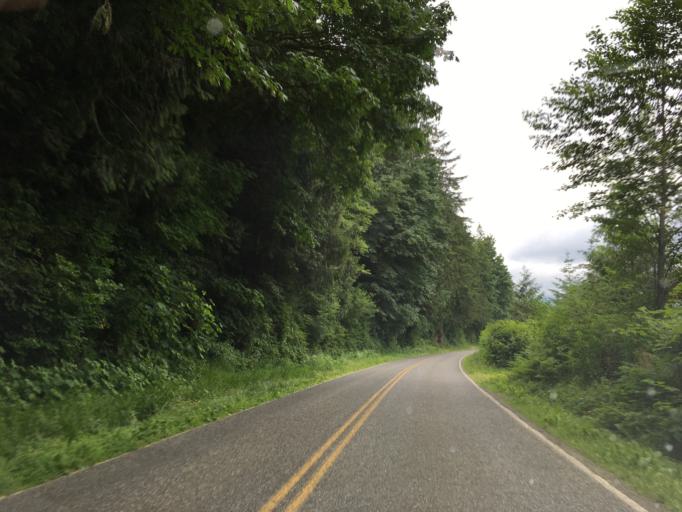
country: US
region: Washington
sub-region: Whatcom County
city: Peaceful Valley
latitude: 48.9952
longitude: -122.0866
